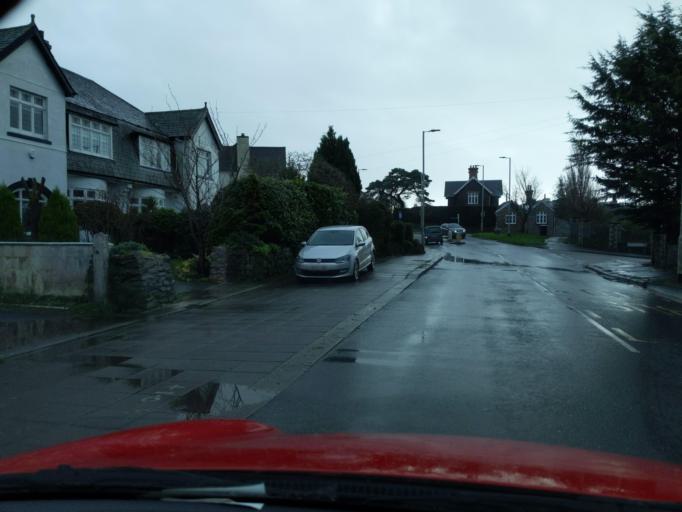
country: GB
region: England
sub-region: Plymouth
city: Plymouth
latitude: 50.3952
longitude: -4.1395
